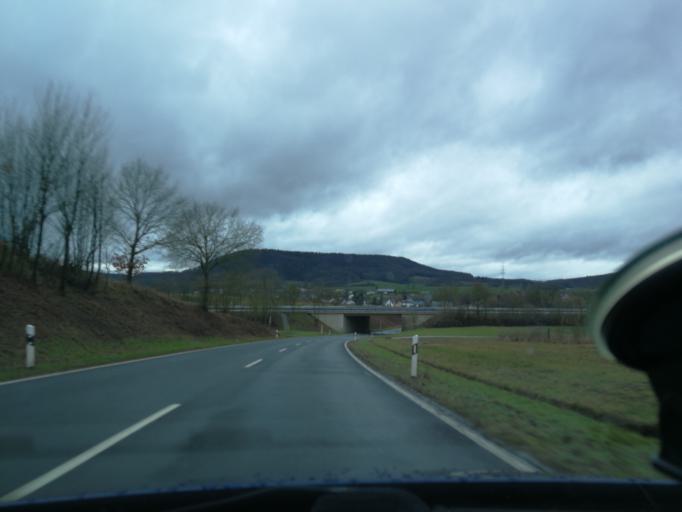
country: DE
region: Rheinland-Pfalz
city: Salmtal
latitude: 49.9218
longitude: 6.8607
